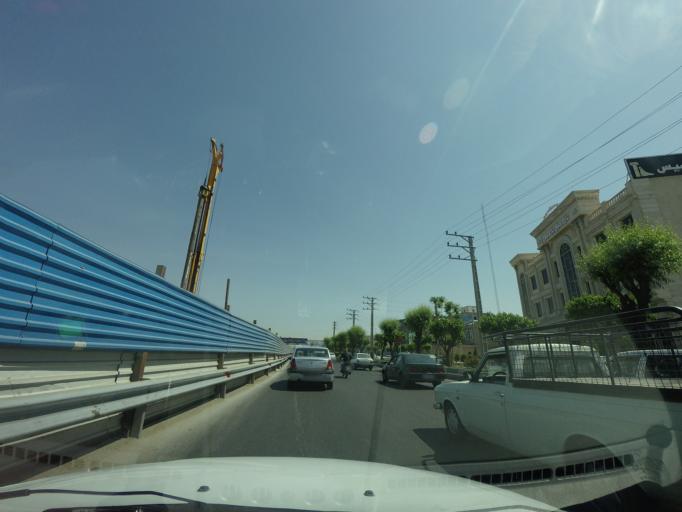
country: IR
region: Tehran
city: Eslamshahr
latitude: 35.6046
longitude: 51.3039
